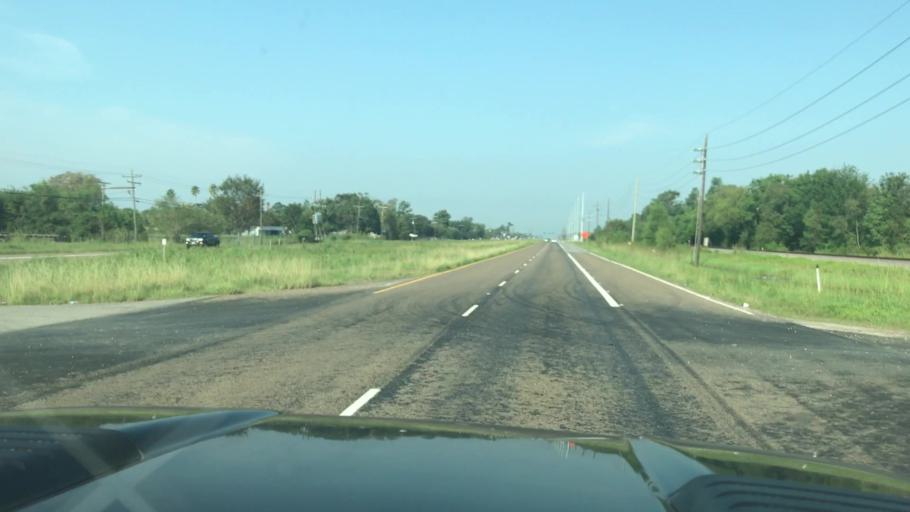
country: US
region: Texas
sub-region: Jefferson County
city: Bevil Oaks
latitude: 30.0634
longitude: -94.2206
